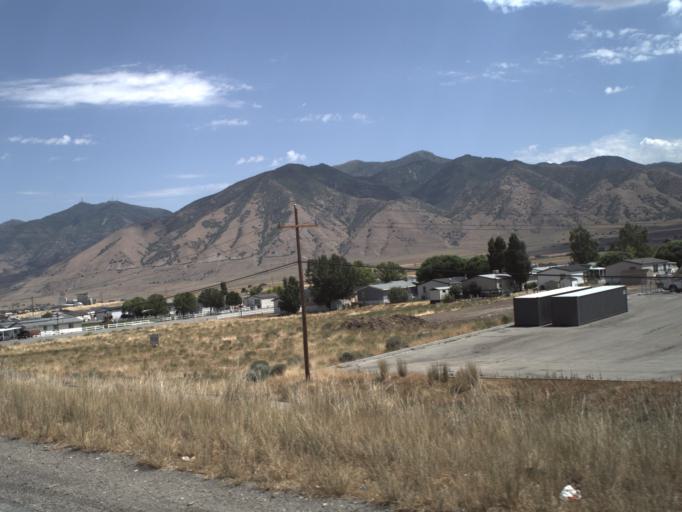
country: US
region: Utah
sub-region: Tooele County
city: Tooele
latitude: 40.5569
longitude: -112.2971
